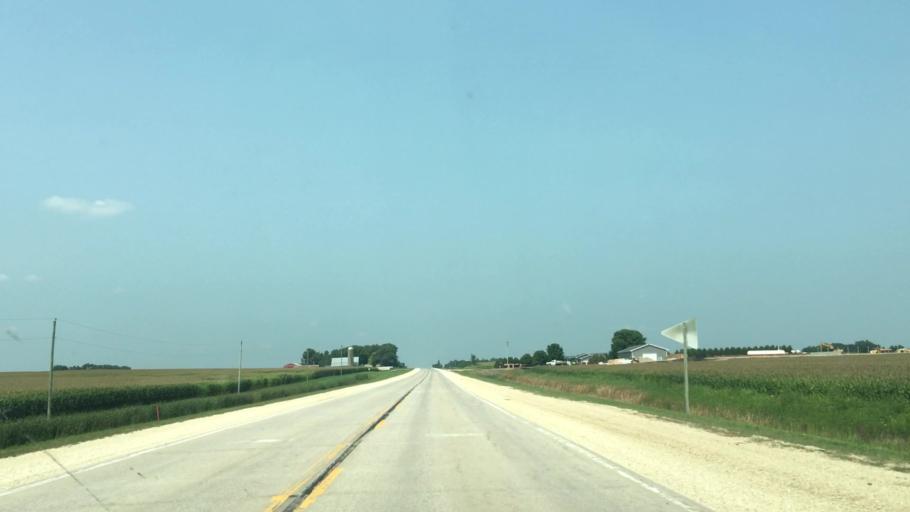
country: US
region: Iowa
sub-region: Fayette County
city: Fayette
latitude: 42.7639
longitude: -91.8045
